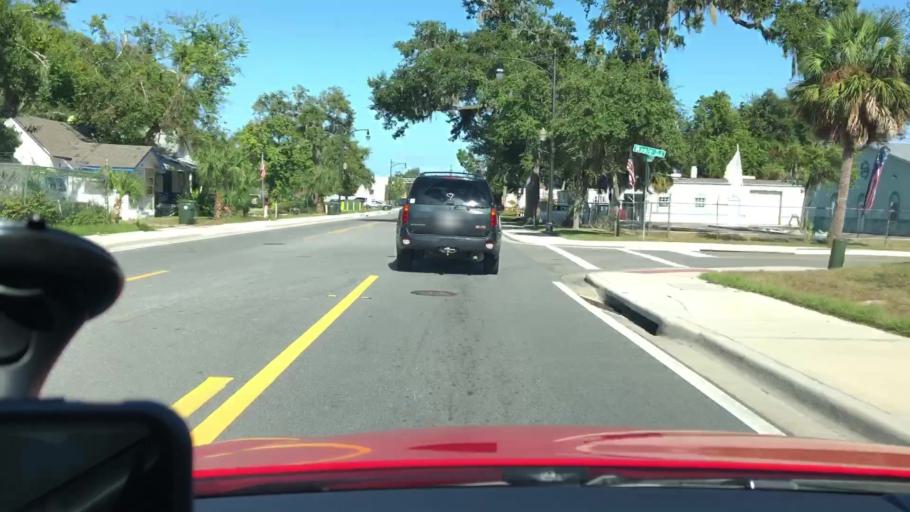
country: US
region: Florida
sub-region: Volusia County
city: Daytona Beach
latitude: 29.2053
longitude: -81.0249
